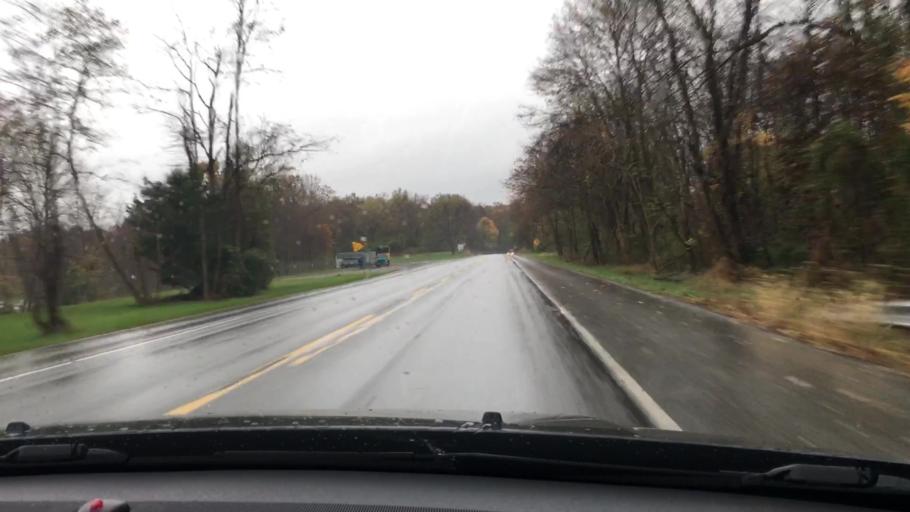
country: US
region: Pennsylvania
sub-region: York County
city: Susquehanna Trails
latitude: 39.8311
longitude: -76.3101
